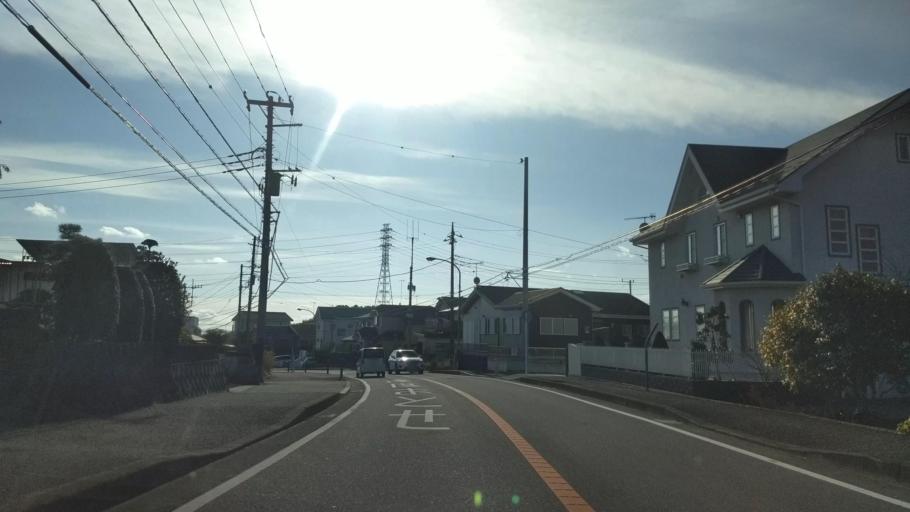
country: JP
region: Kanagawa
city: Hadano
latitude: 35.3916
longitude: 139.2351
